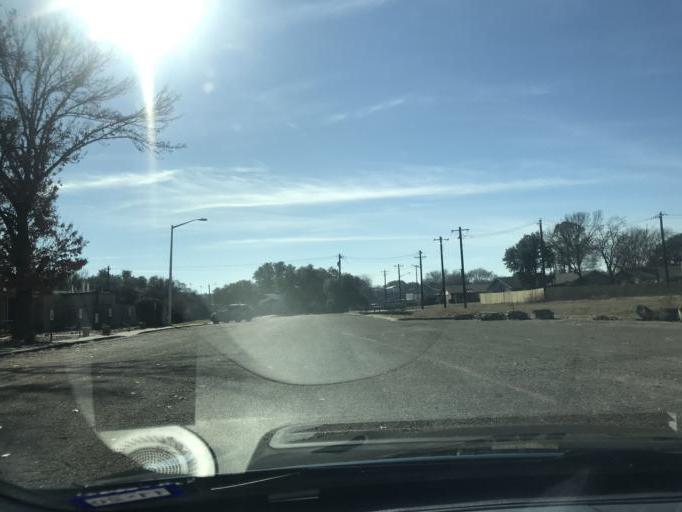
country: US
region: Texas
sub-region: Denton County
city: Denton
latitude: 33.2277
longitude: -97.1443
